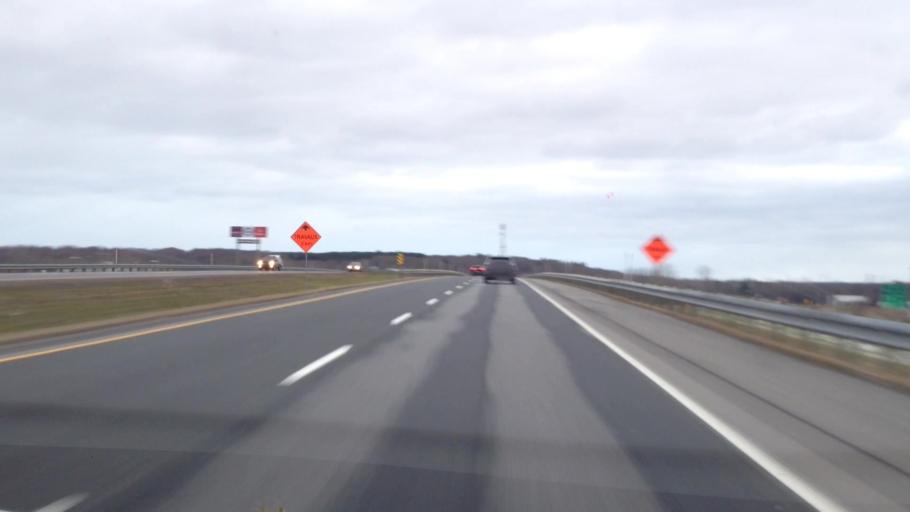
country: CA
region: Quebec
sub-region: Monteregie
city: Rigaud
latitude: 45.4611
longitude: -74.2307
